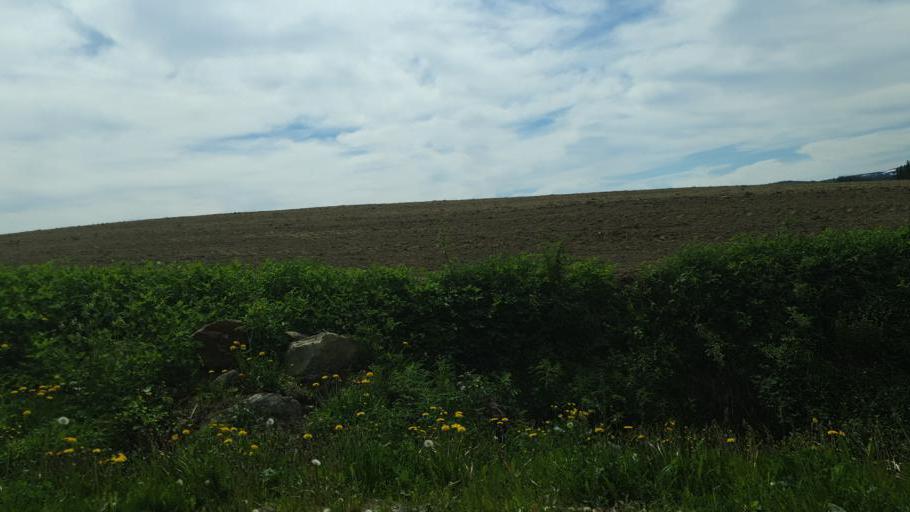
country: NO
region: Nord-Trondelag
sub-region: Leksvik
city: Leksvik
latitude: 63.6849
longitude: 10.5744
